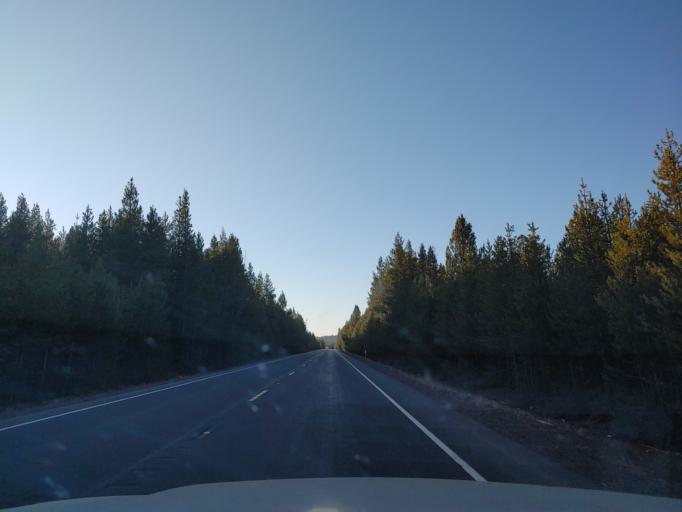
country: US
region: Oregon
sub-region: Deschutes County
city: La Pine
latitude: 43.4096
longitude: -121.8302
